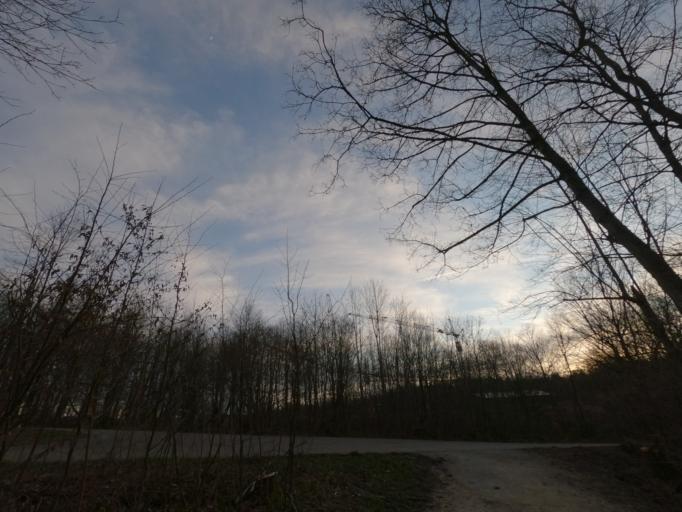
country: DE
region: Baden-Wuerttemberg
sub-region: Regierungsbezirk Stuttgart
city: Eislingen
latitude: 48.7180
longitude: 9.6894
